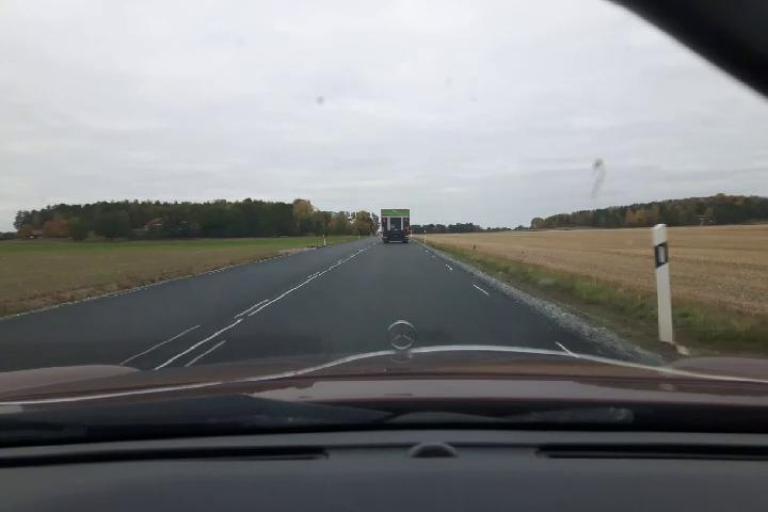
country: SE
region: Uppsala
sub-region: Enkopings Kommun
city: Enkoping
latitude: 59.6021
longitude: 17.0200
